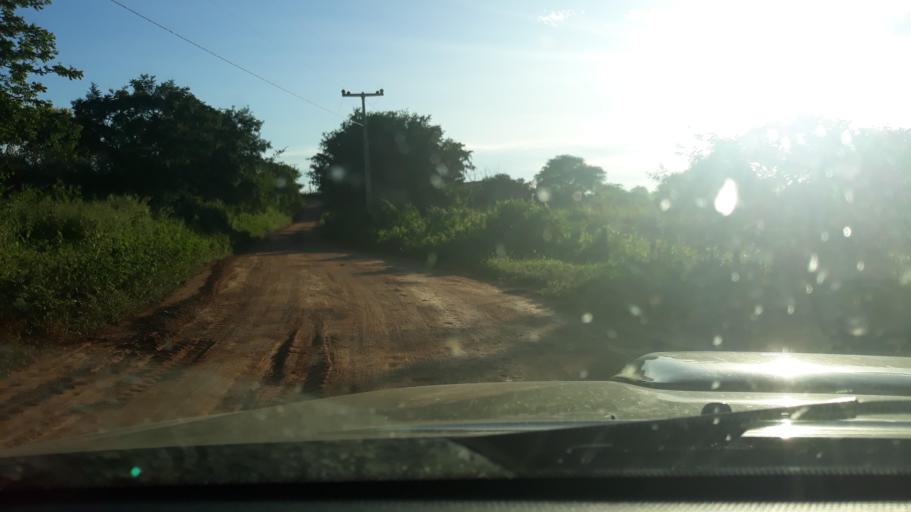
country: BR
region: Bahia
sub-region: Riacho De Santana
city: Riacho de Santana
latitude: -13.8404
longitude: -42.7363
